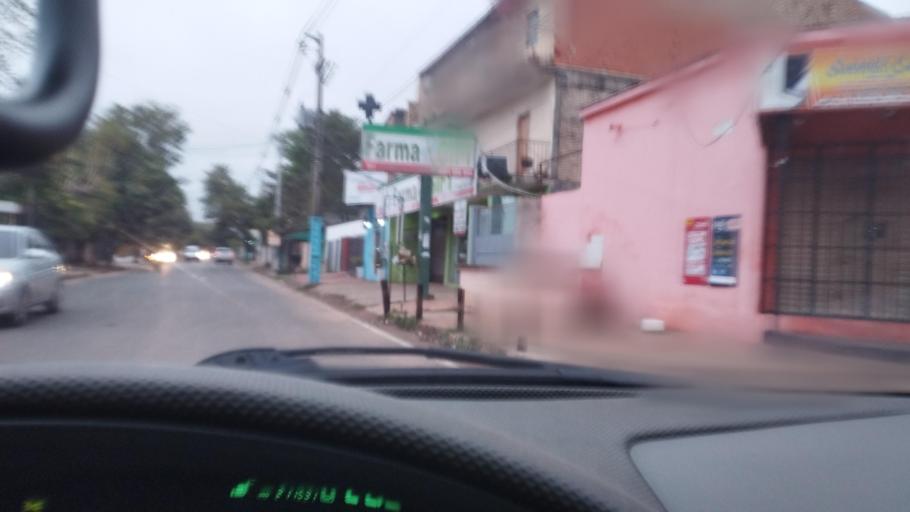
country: PY
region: Central
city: Fernando de la Mora
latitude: -25.3008
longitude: -57.5301
